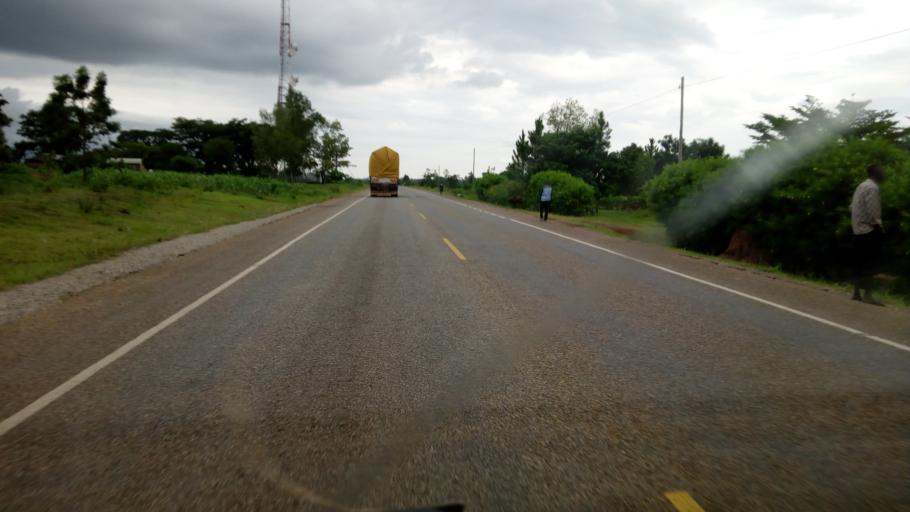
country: UG
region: Eastern Region
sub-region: Tororo District
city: Tororo
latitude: 0.8063
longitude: 34.1700
